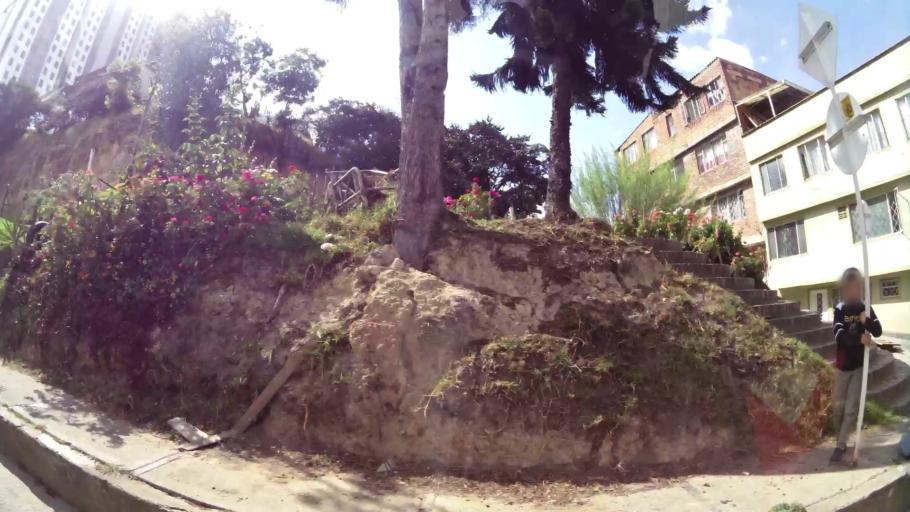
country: CO
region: Bogota D.C.
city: Bogota
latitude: 4.5648
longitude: -74.1041
